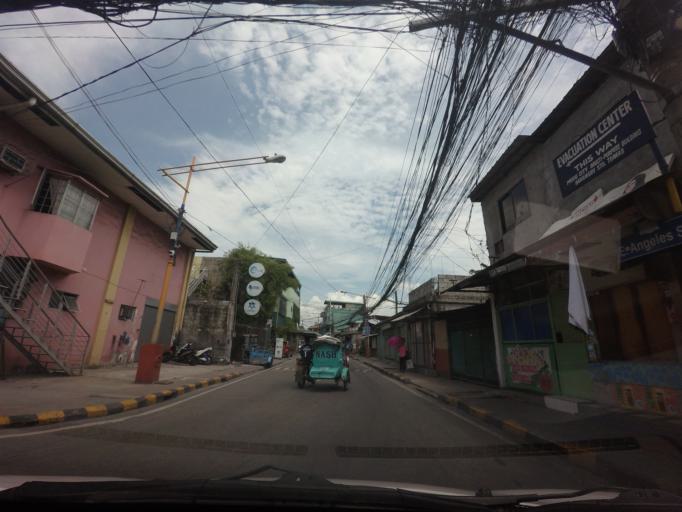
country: PH
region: Calabarzon
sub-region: Province of Rizal
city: Pateros
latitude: 14.5630
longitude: 121.0818
